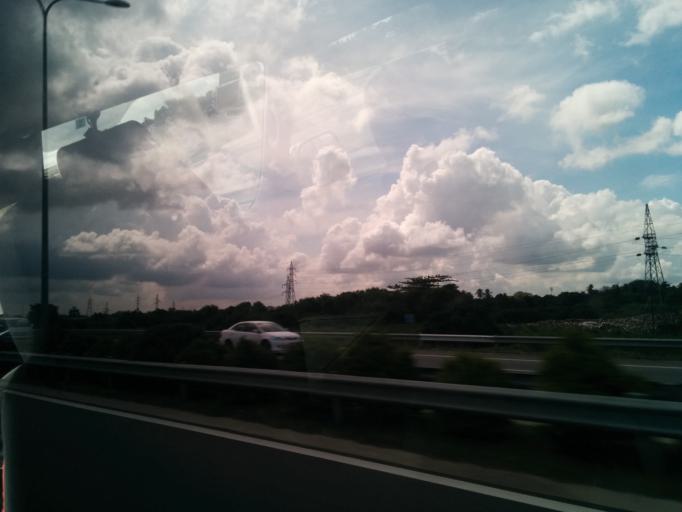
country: LK
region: Western
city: Peliyagoda
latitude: 6.9656
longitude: 79.8915
